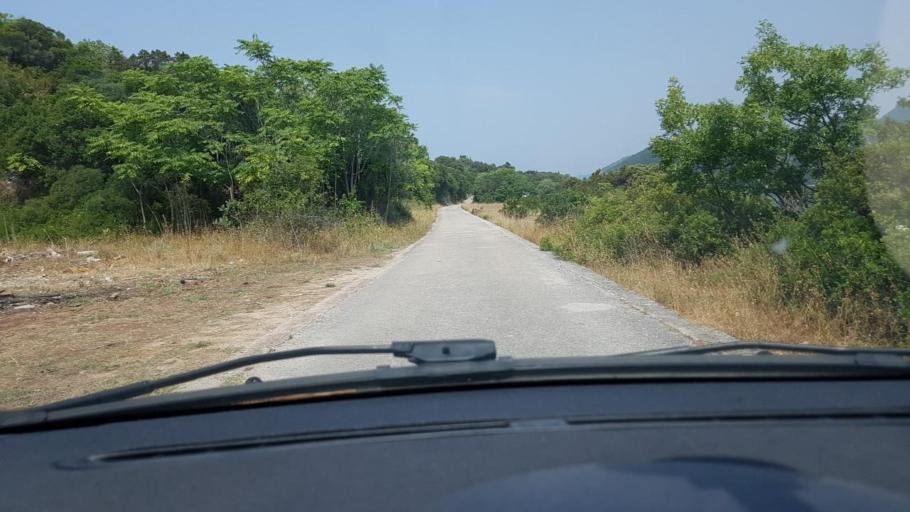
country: ME
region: Herceg Novi
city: Herceg-Novi
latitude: 42.3970
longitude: 18.5248
